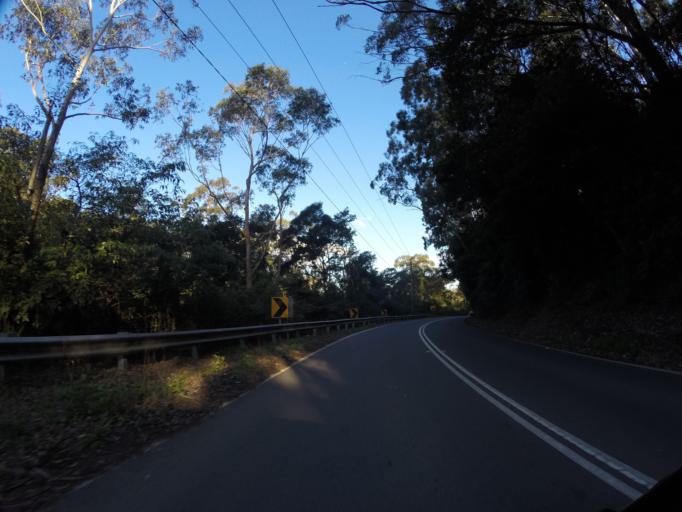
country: AU
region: New South Wales
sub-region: Wollongong
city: Cordeaux Heights
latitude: -34.4366
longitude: 150.8371
